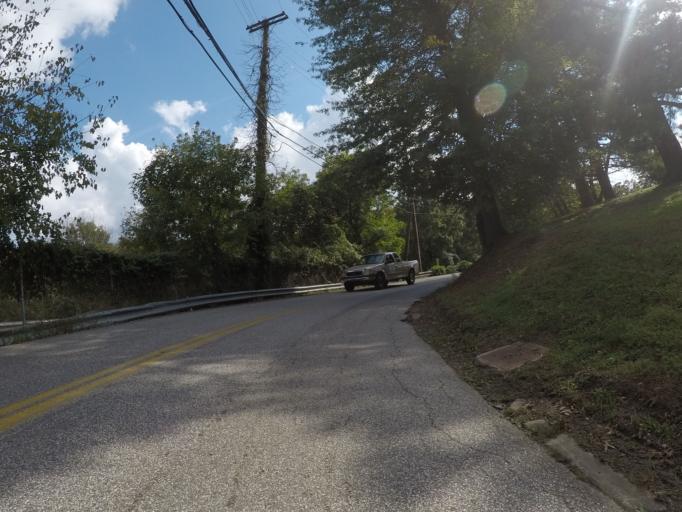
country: US
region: West Virginia
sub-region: Cabell County
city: Huntington
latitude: 38.4037
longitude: -82.4380
